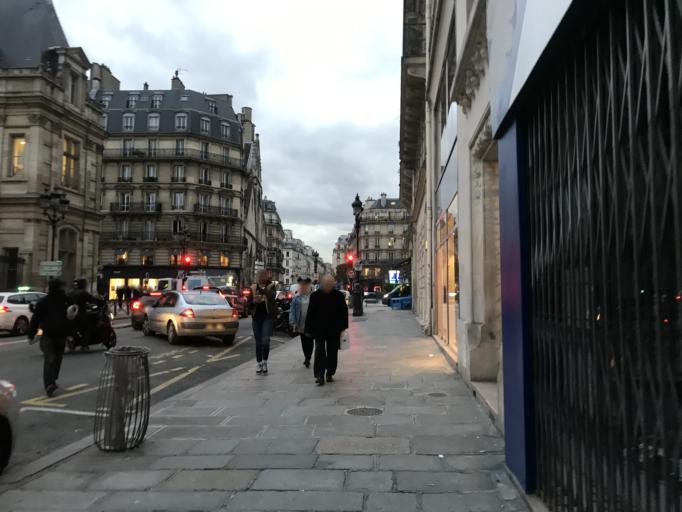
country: FR
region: Ile-de-France
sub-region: Paris
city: Paris
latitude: 48.8665
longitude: 2.3540
